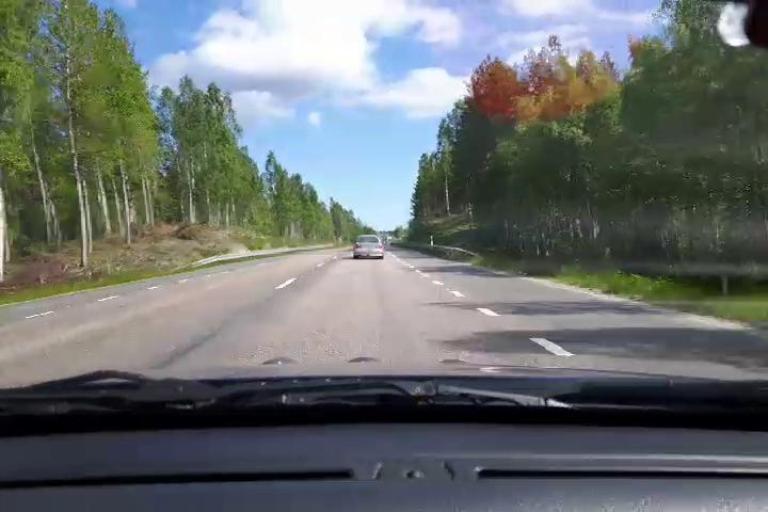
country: SE
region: Gaevleborg
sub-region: Hudiksvalls Kommun
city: Sorforsa
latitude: 61.7191
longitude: 17.0249
